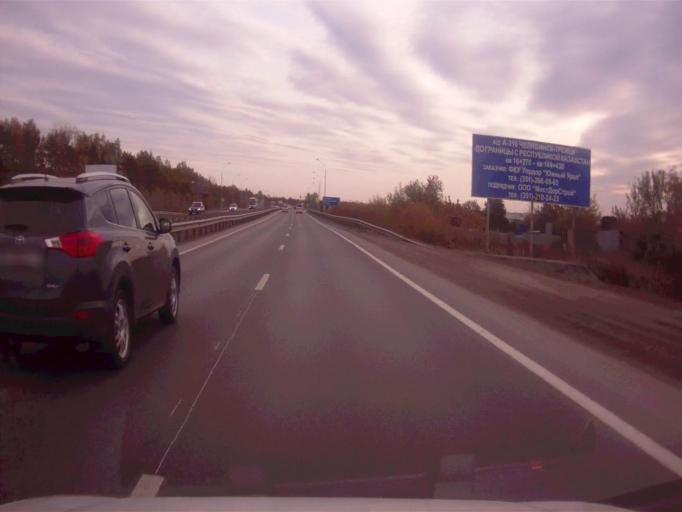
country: RU
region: Chelyabinsk
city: Novosineglazovskiy
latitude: 55.0343
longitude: 61.4429
